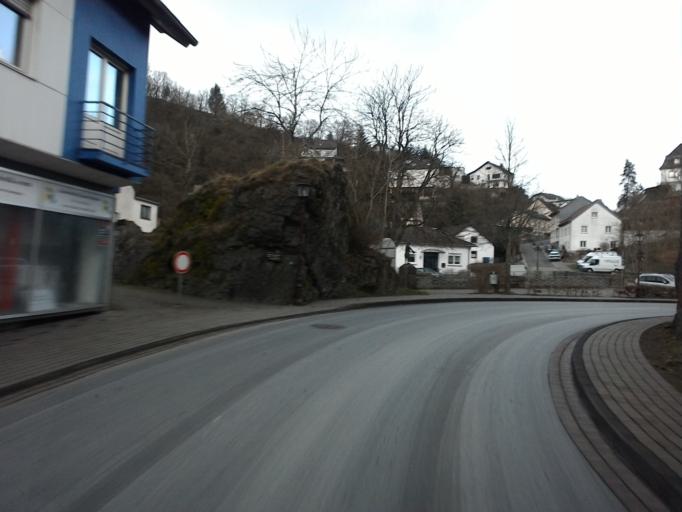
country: DE
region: Rheinland-Pfalz
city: Scheuern
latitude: 50.0127
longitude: 6.2907
